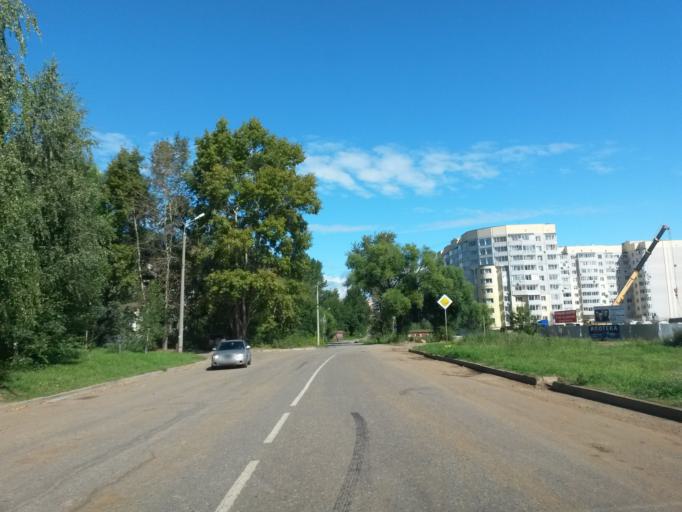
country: RU
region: Jaroslavl
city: Yaroslavl
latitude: 57.5869
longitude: 39.8657
